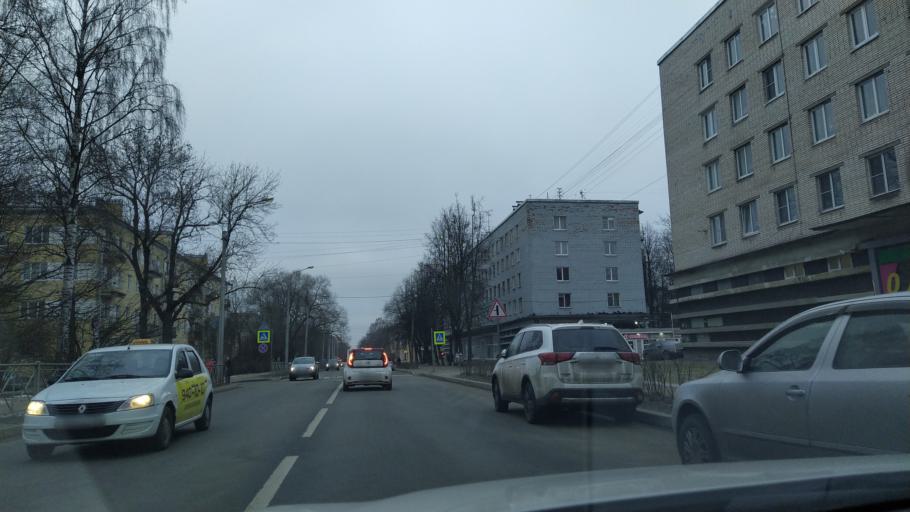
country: RU
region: St.-Petersburg
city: Pushkin
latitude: 59.7244
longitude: 30.4147
